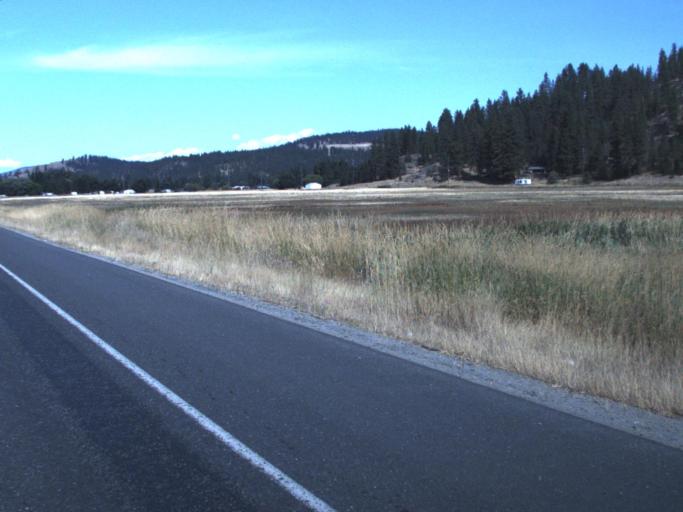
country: US
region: Washington
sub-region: Stevens County
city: Colville
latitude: 48.4445
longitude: -117.8697
